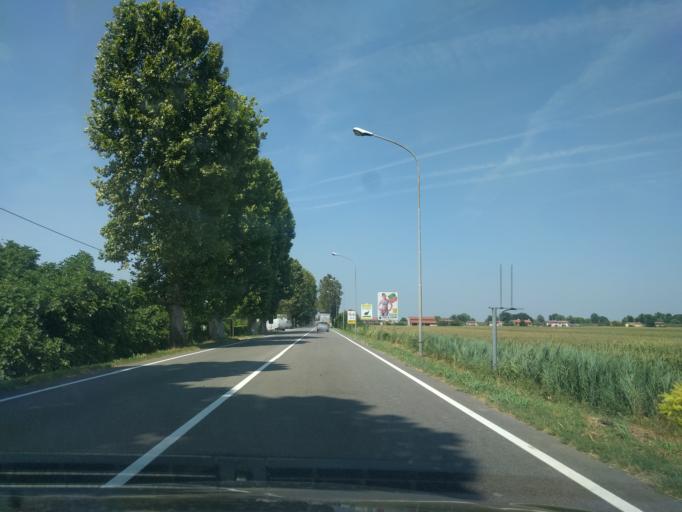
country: IT
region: Veneto
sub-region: Provincia di Padova
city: Stanghella
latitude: 45.1390
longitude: 11.7569
